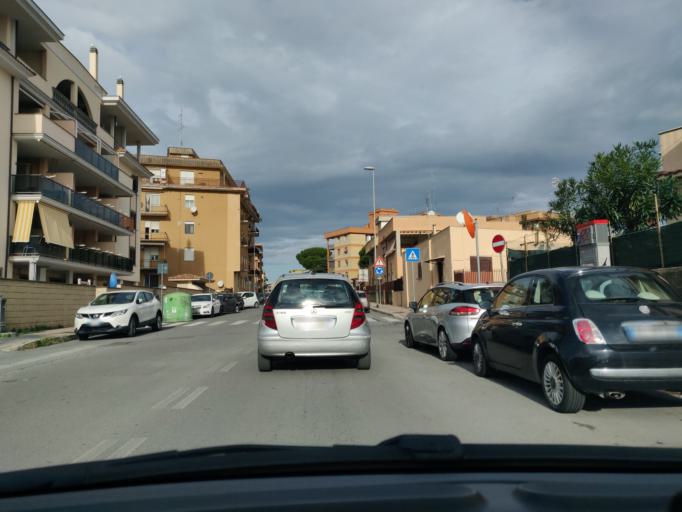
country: IT
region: Latium
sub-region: Citta metropolitana di Roma Capitale
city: Civitavecchia
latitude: 42.0912
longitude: 11.8071
